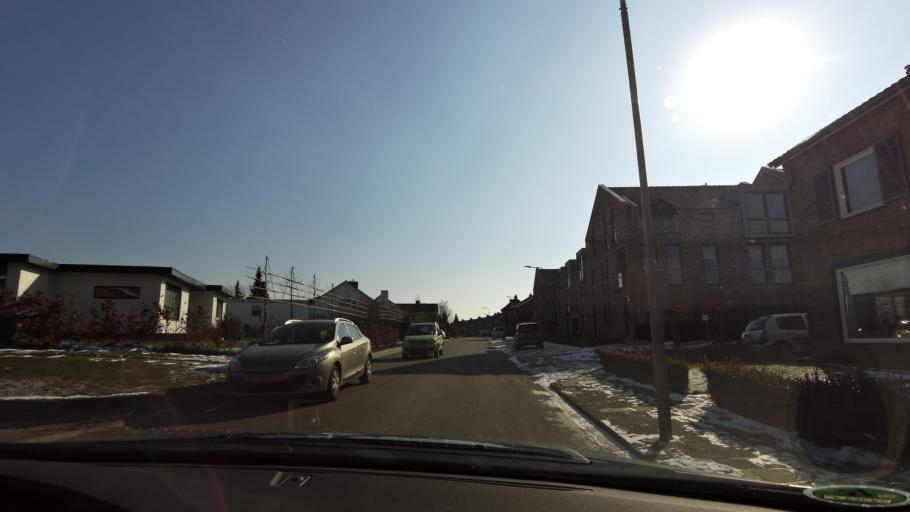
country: NL
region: Limburg
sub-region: Valkenburg aan de Geul
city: Berg
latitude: 50.8626
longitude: 5.7843
